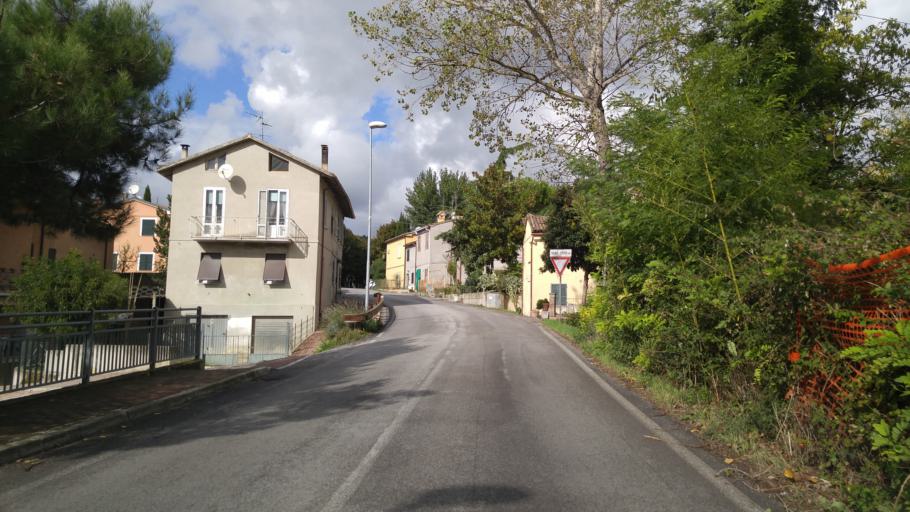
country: IT
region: The Marches
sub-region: Provincia di Pesaro e Urbino
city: Mombaroccio
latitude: 43.8401
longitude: 12.8948
